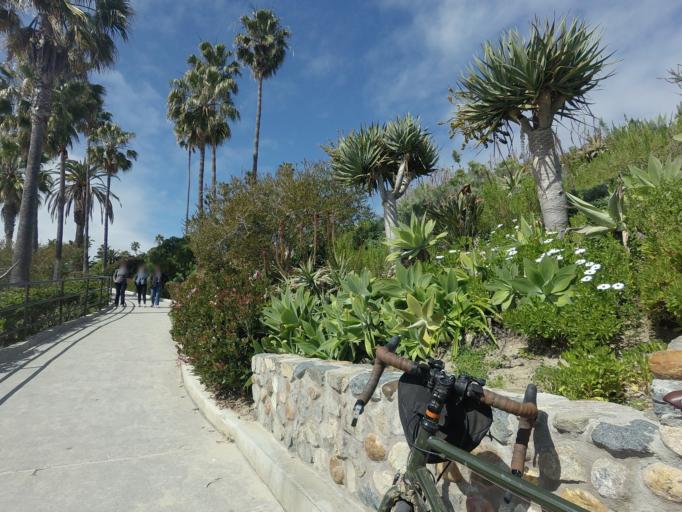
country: US
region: California
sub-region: Orange County
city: Laguna Beach
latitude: 33.5429
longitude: -117.7883
